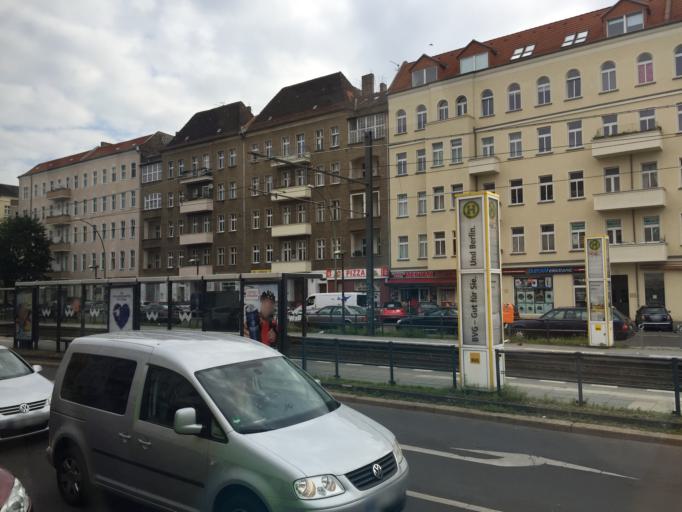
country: DE
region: Berlin
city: Friedrichshain Bezirk
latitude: 52.5224
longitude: 13.4502
